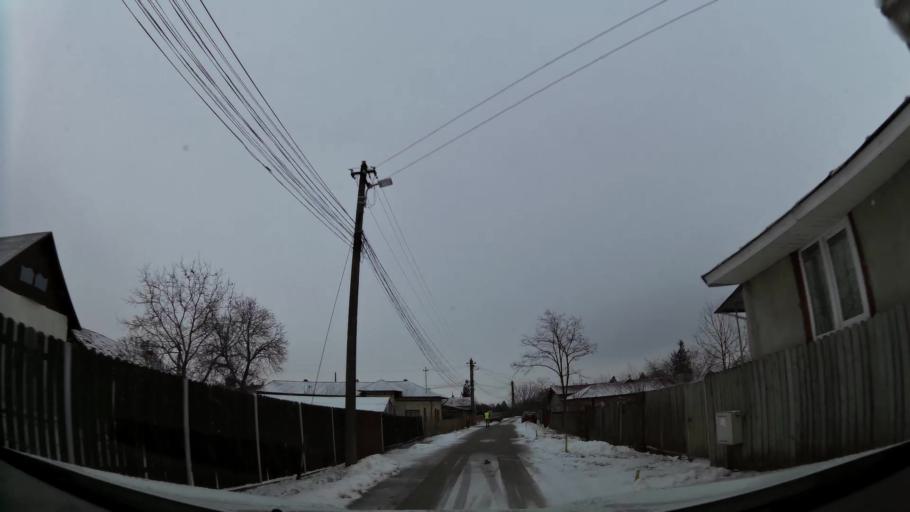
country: RO
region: Prahova
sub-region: Comuna Berceni
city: Corlatesti
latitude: 44.9160
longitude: 26.0834
